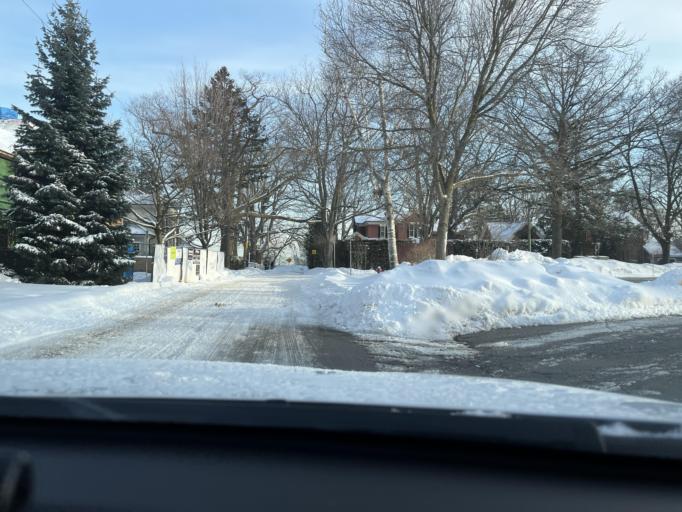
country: CA
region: Ontario
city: Oakville
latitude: 43.4478
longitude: -79.6628
